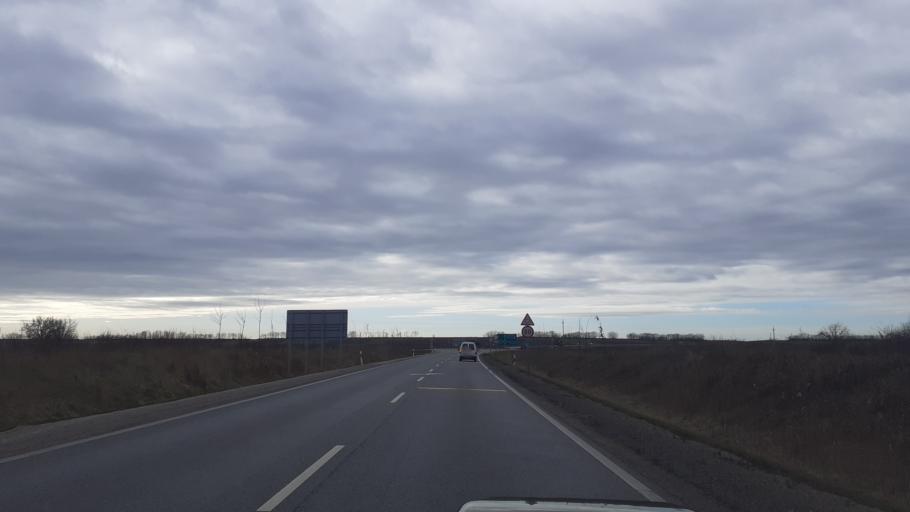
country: HU
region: Fejer
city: Seregelyes
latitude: 47.0951
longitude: 18.5957
